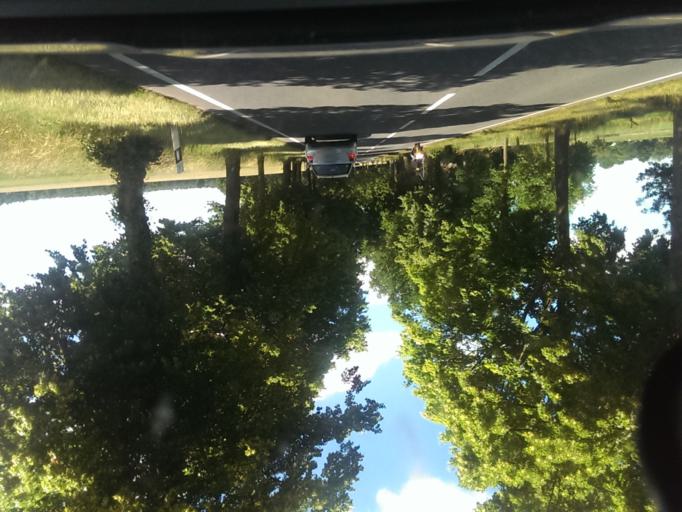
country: DE
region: Lower Saxony
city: Verden
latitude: 52.9808
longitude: 9.2602
